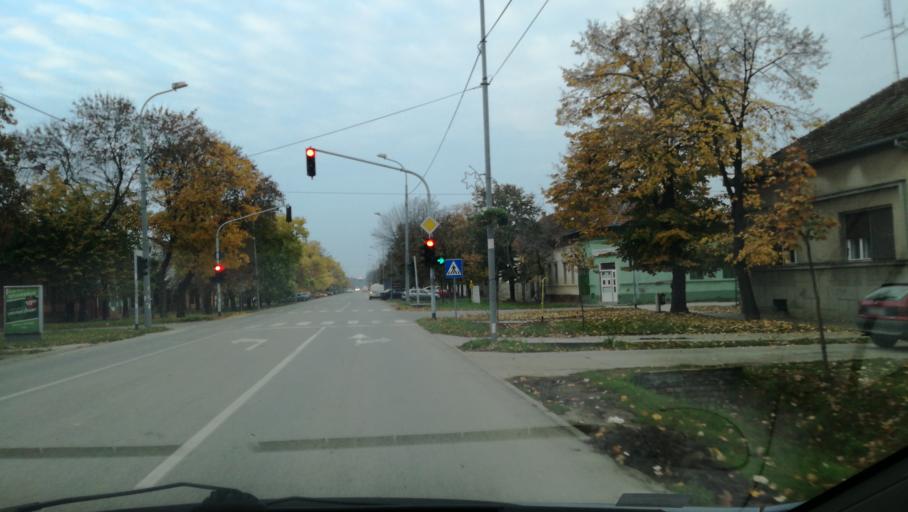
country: RS
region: Autonomna Pokrajina Vojvodina
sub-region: Severnobanatski Okrug
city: Kikinda
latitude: 45.8251
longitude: 20.4574
